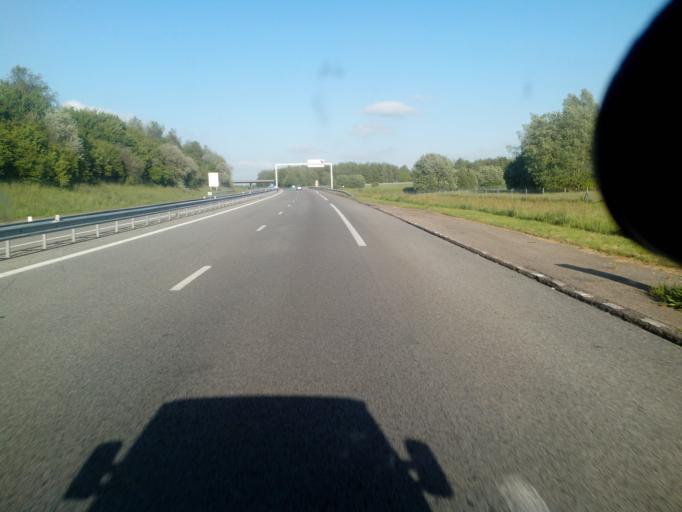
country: FR
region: Haute-Normandie
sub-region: Departement de la Seine-Maritime
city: Yerville
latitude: 49.6527
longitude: 0.8378
